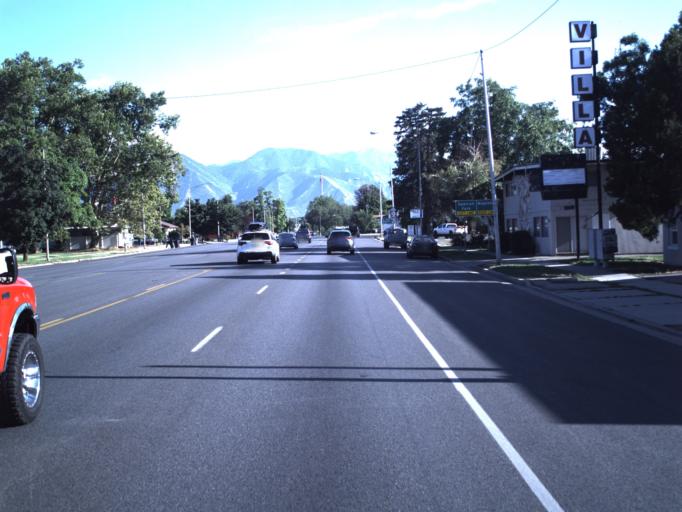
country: US
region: Utah
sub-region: Utah County
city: Springville
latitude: 40.1602
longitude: -111.6108
